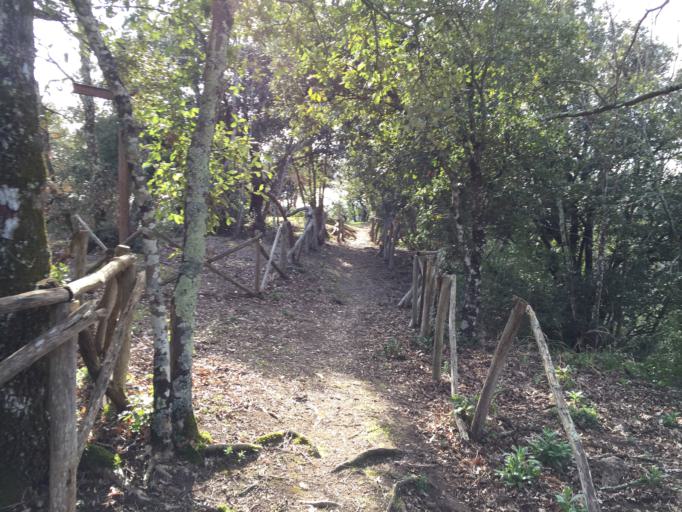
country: IT
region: Latium
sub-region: Provincia di Viterbo
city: Calcata Nuova
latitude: 42.2121
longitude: 12.4191
